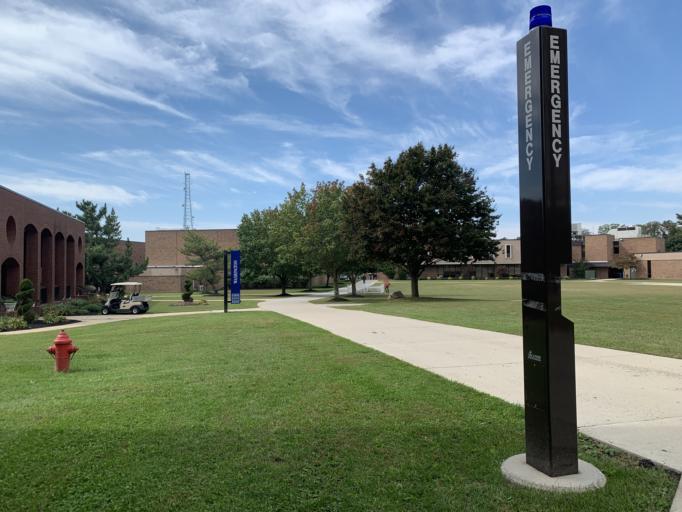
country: US
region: New Jersey
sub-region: Gloucester County
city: Turnersville
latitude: 39.7846
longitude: -75.0386
